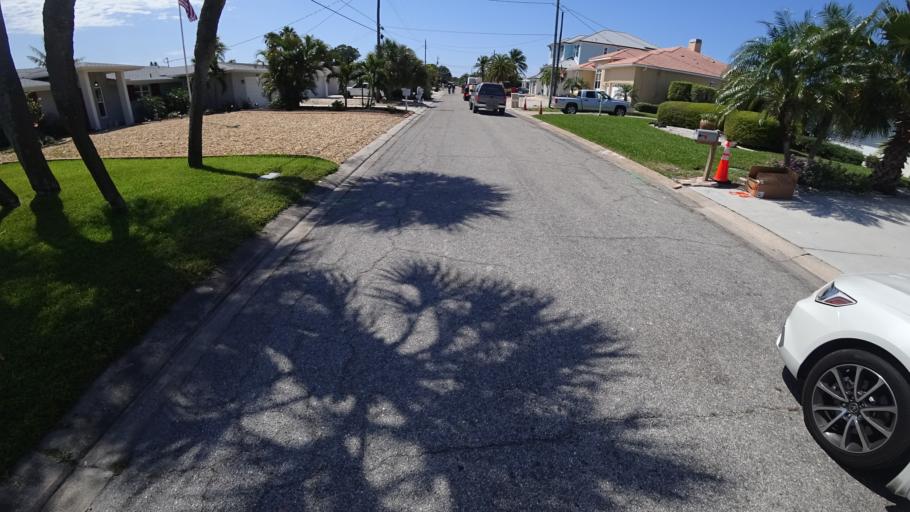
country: US
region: Florida
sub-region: Manatee County
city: Cortez
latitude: 27.4677
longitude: -82.6628
